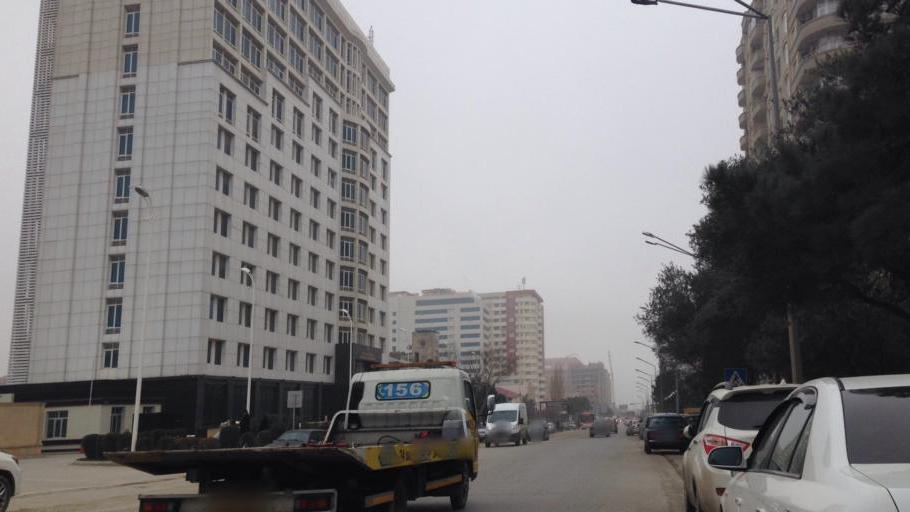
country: AZ
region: Baki
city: Baku
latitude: 40.3864
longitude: 49.8762
